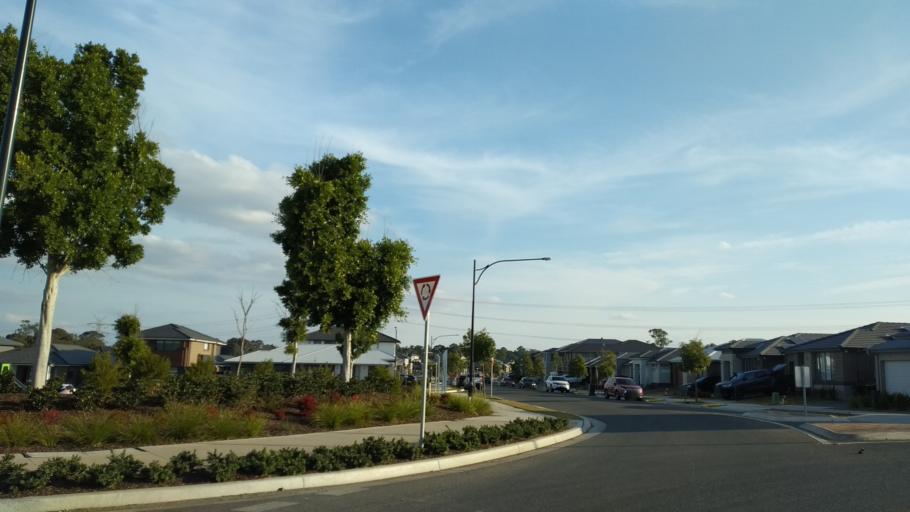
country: AU
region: New South Wales
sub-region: Penrith Municipality
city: Werrington County
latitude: -33.7357
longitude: 150.7535
